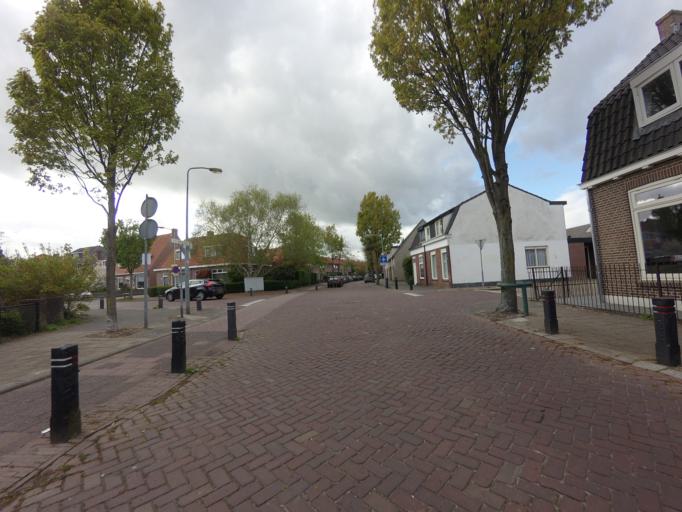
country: NL
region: Utrecht
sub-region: Gemeente Zeist
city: Zeist
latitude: 52.0885
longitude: 5.2354
